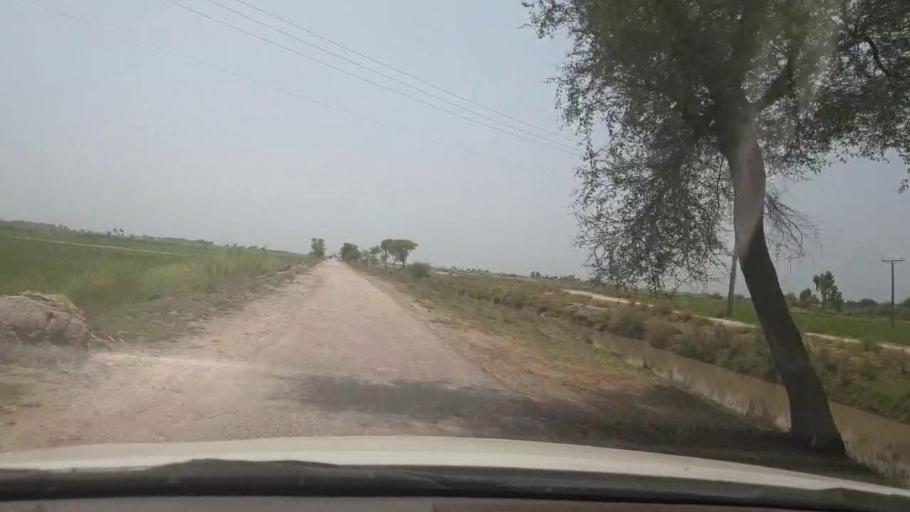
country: PK
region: Sindh
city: Shikarpur
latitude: 28.0505
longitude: 68.5850
